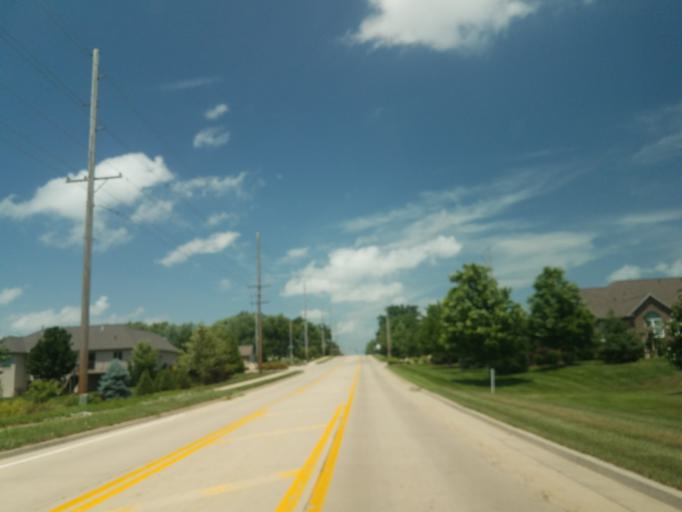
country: US
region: Illinois
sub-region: McLean County
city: Bloomington
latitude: 40.4468
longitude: -89.0056
